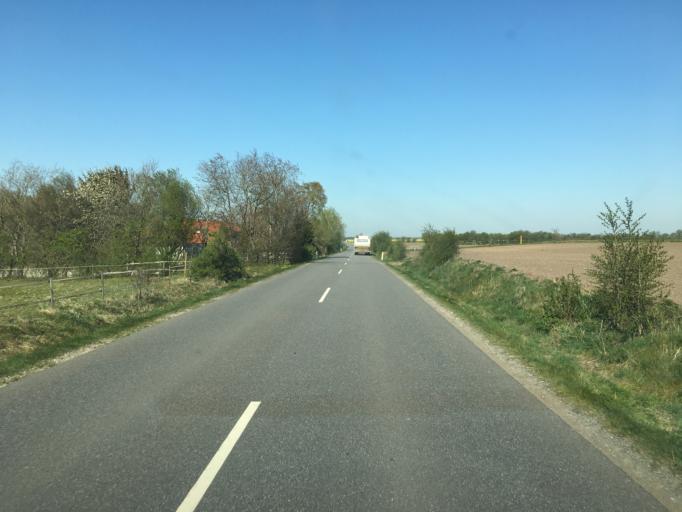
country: DK
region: South Denmark
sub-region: Aabenraa Kommune
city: Rodekro
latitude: 55.0014
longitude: 9.3055
